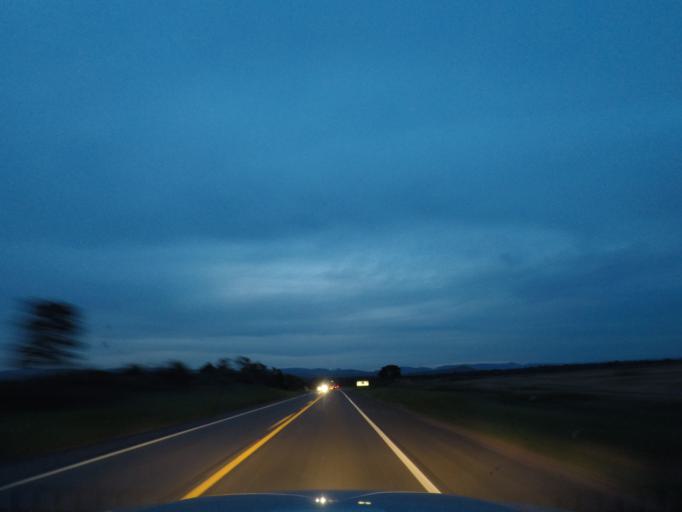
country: BR
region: Bahia
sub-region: Andarai
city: Vera Cruz
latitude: -12.4954
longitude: -41.3010
